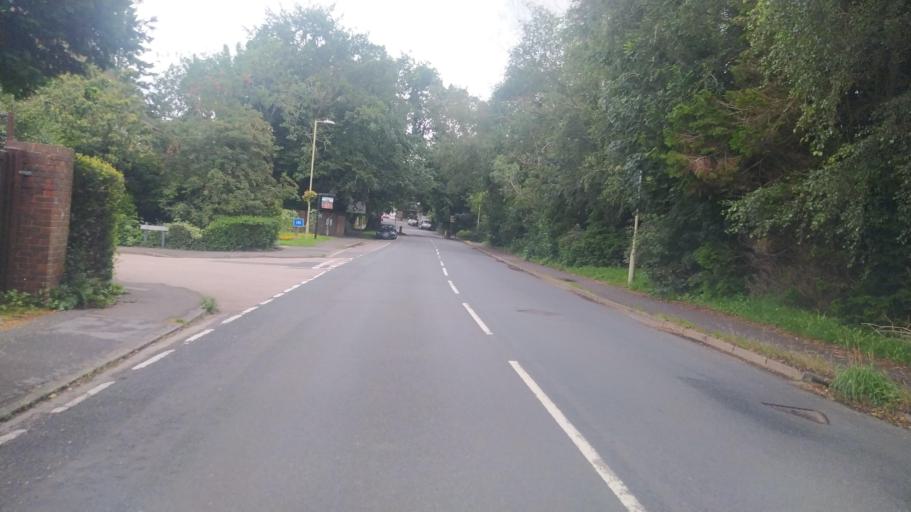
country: GB
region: England
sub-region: Hampshire
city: Liphook
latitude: 51.0746
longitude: -0.8032
